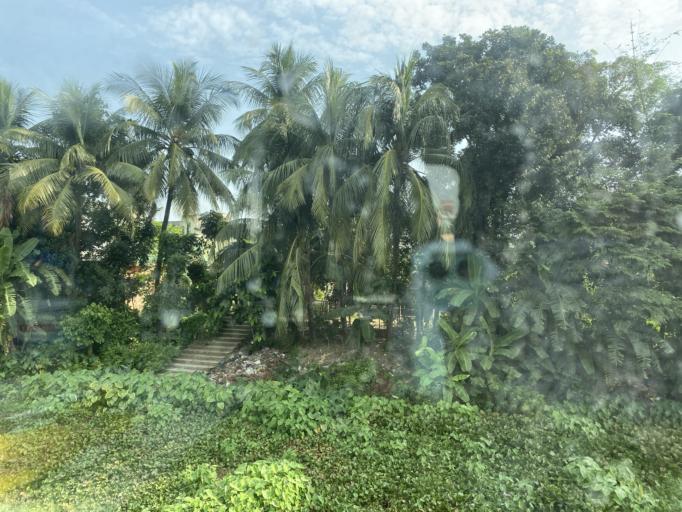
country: BD
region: Dhaka
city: Bhairab Bazar
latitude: 23.9645
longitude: 91.1172
